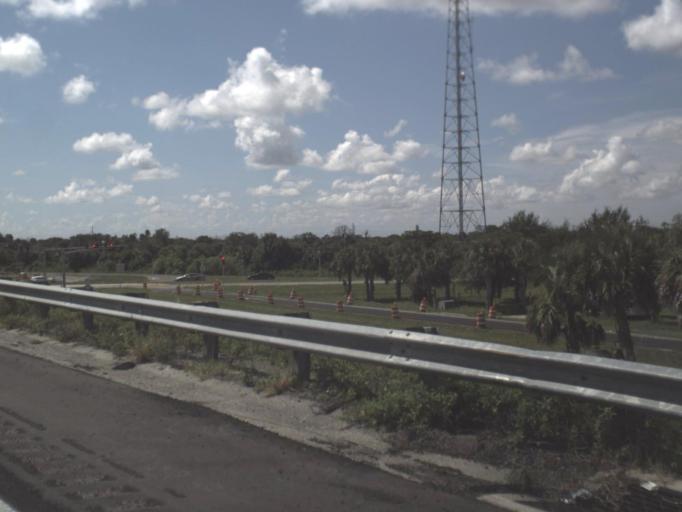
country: US
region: Florida
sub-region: Lee County
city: Tice
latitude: 26.7164
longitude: -81.8130
